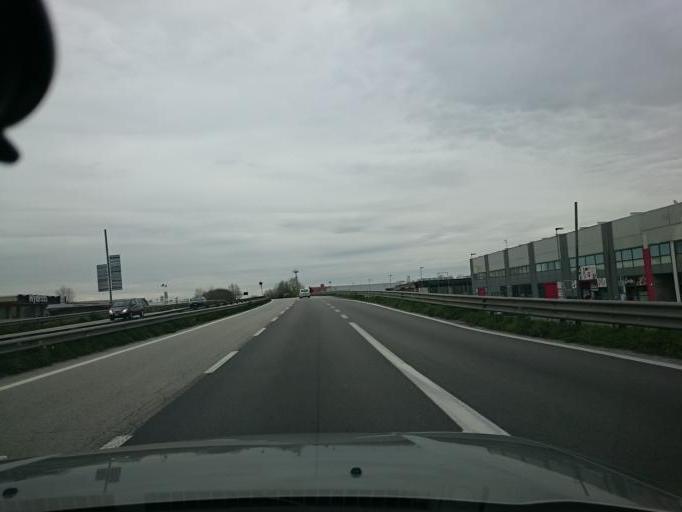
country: IT
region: Veneto
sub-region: Provincia di Padova
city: Noventa
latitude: 45.3989
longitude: 11.9302
